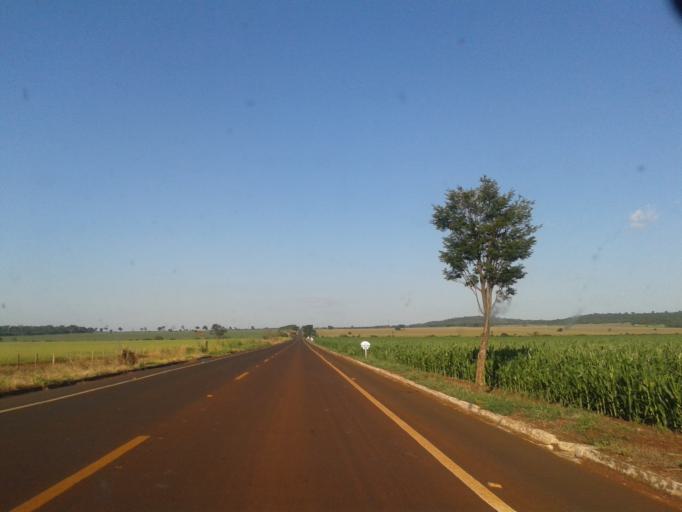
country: BR
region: Minas Gerais
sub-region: Capinopolis
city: Capinopolis
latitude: -18.7121
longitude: -49.8266
